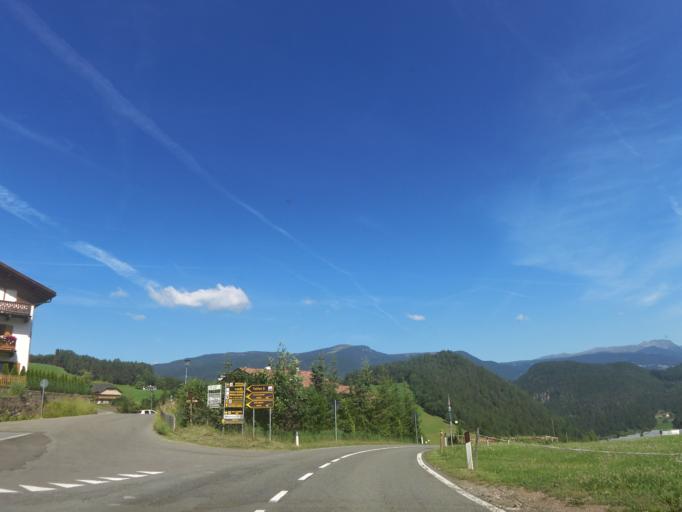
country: IT
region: Trentino-Alto Adige
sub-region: Bolzano
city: Castelrotto
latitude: 46.5571
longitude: 11.5557
